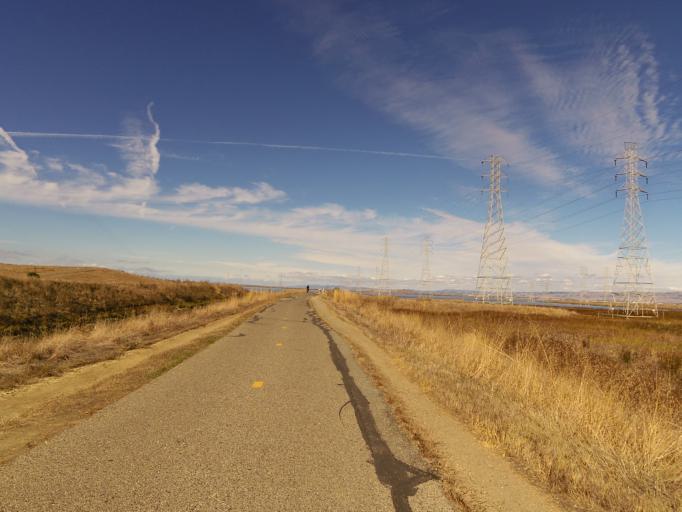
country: US
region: California
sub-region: Santa Clara County
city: Mountain View
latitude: 37.4339
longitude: -122.0712
